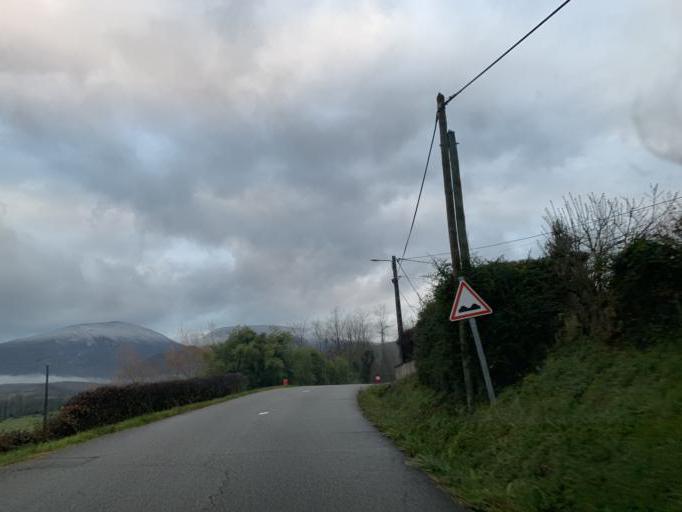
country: FR
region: Rhone-Alpes
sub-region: Departement de l'Ain
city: Belley
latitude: 45.7933
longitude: 5.6905
